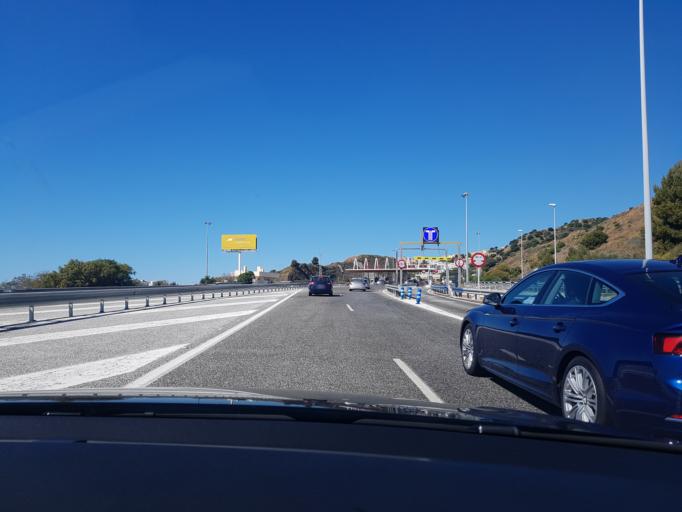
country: ES
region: Andalusia
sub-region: Provincia de Malaga
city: Fuengirola
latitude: 36.5054
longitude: -4.7152
